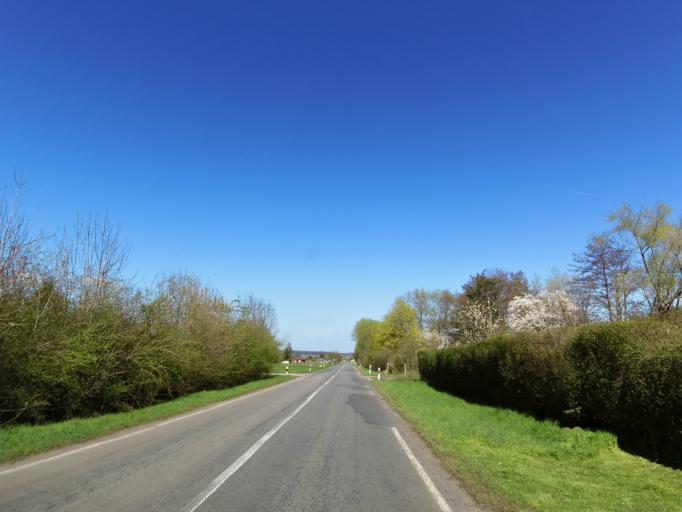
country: DE
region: Thuringia
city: Waltershausen
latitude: 50.8871
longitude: 10.5809
